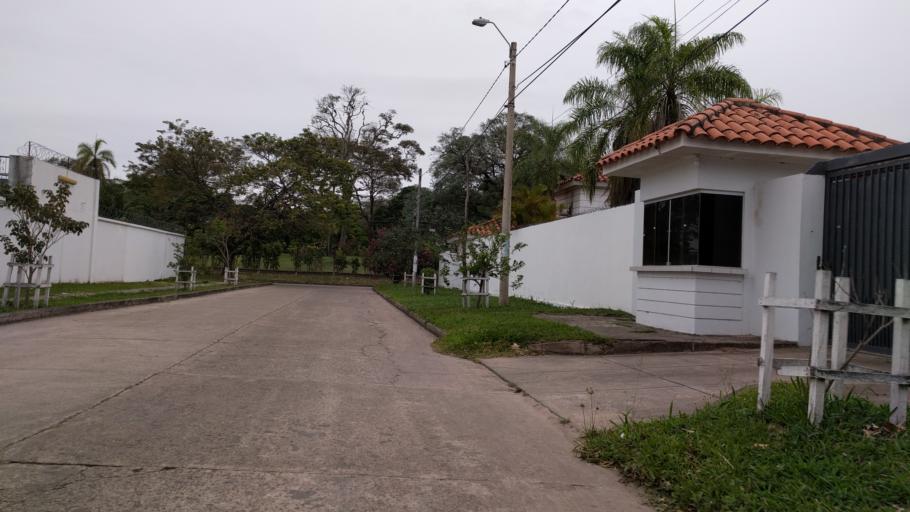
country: BO
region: Santa Cruz
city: Santa Cruz de la Sierra
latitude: -17.7989
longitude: -63.2122
